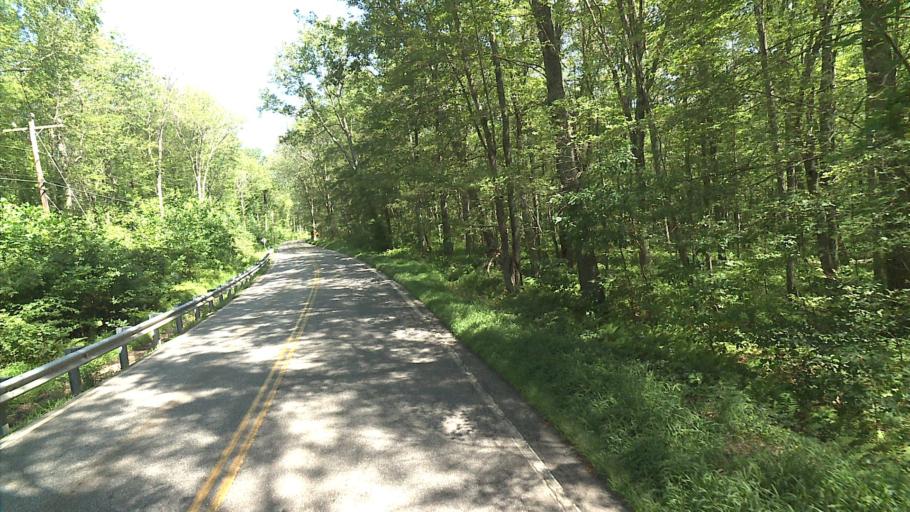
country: US
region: Connecticut
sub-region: Windham County
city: Windham
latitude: 41.7511
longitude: -72.0630
